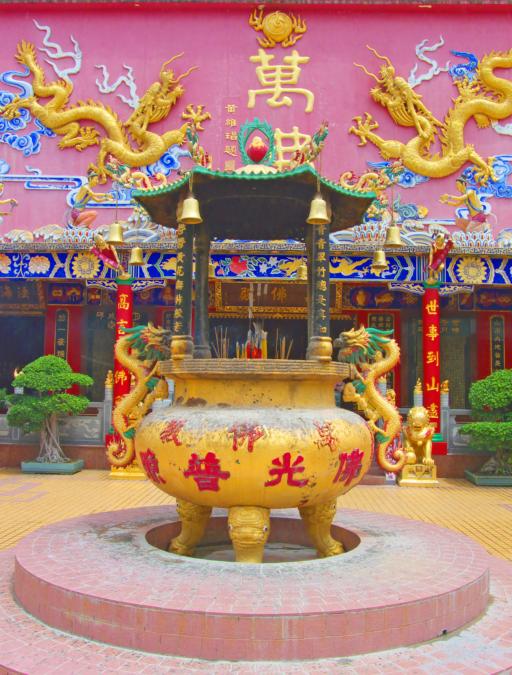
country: HK
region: Sha Tin
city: Sha Tin
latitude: 22.3875
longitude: 114.1848
